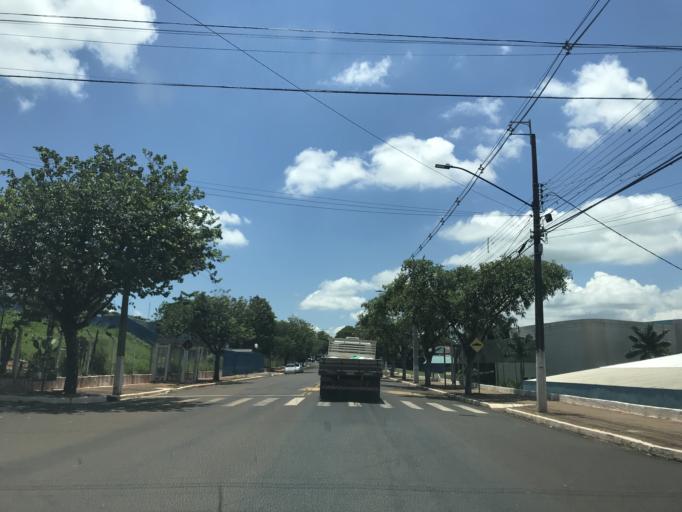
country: BR
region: Parana
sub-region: Marialva
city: Marialva
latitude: -23.4901
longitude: -51.7891
